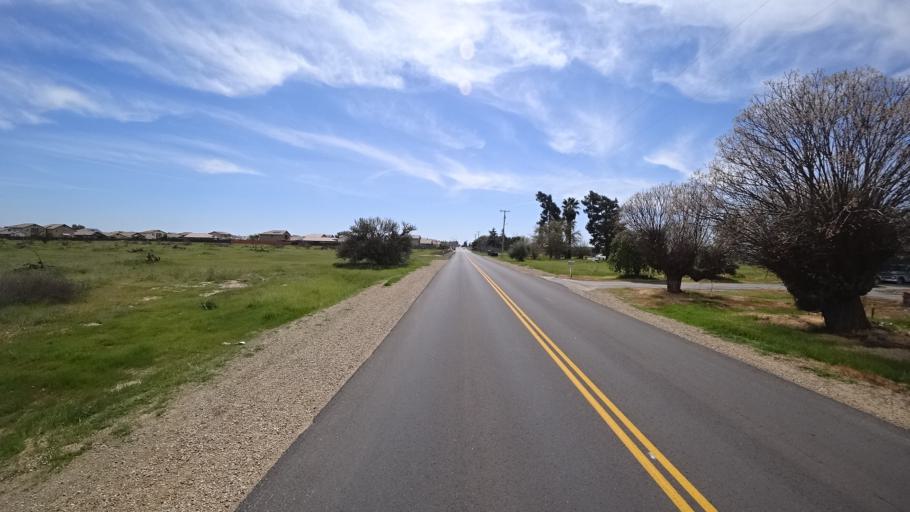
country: US
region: California
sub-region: Fresno County
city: Biola
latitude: 36.8196
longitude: -119.9257
